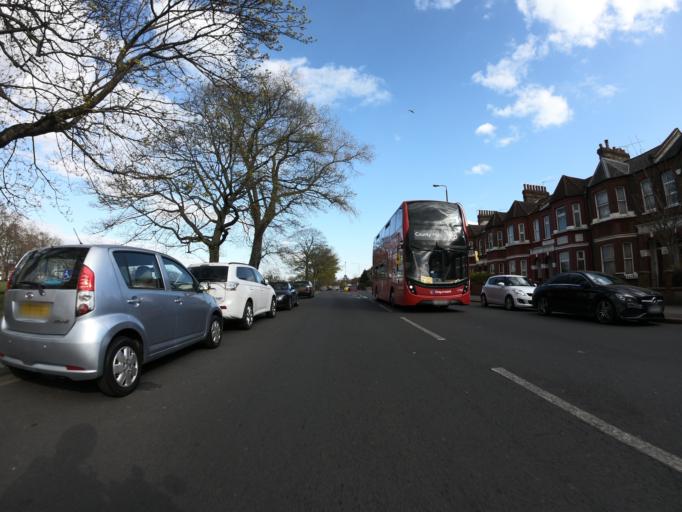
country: GB
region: England
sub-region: Greater London
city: Woolwich
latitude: 51.4806
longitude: 0.0817
